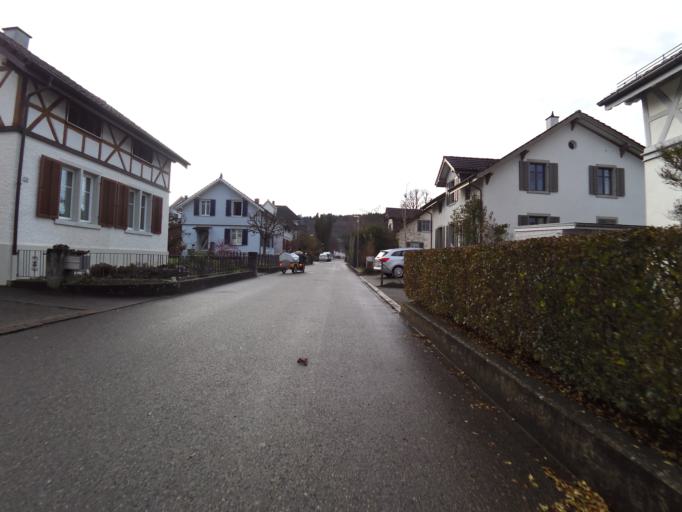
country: CH
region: Thurgau
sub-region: Frauenfeld District
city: Frauenfeld
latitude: 47.5515
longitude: 8.8909
